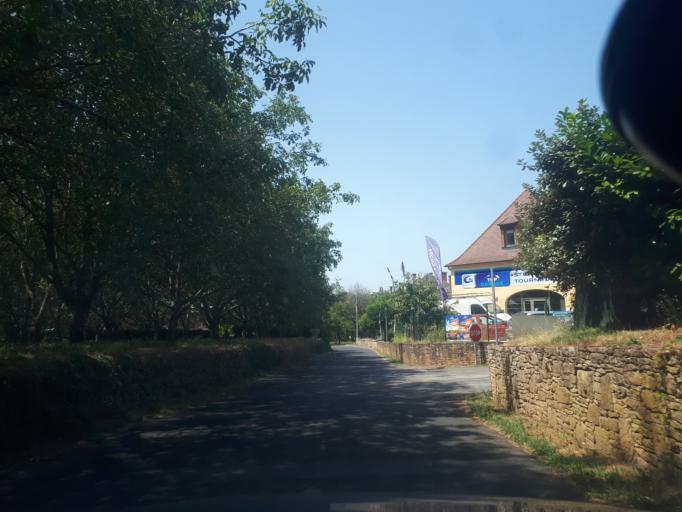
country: FR
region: Midi-Pyrenees
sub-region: Departement du Lot
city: Gourdon
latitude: 44.8334
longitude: 1.3914
